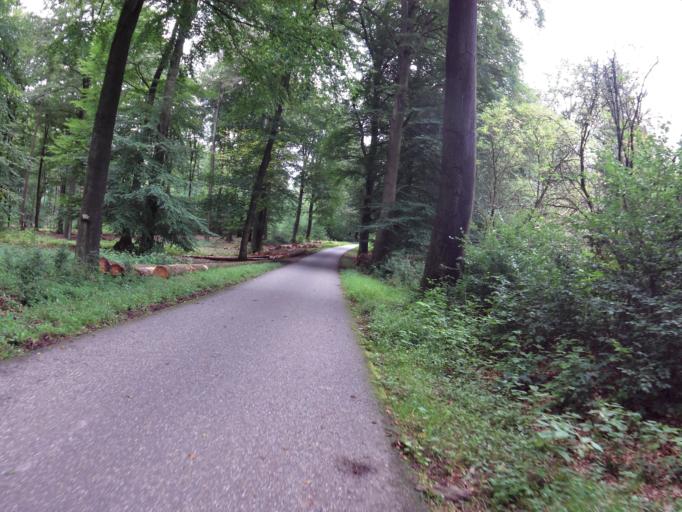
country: NL
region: Gelderland
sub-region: Gemeente Rheden
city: Ellecom
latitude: 52.0408
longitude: 6.0875
